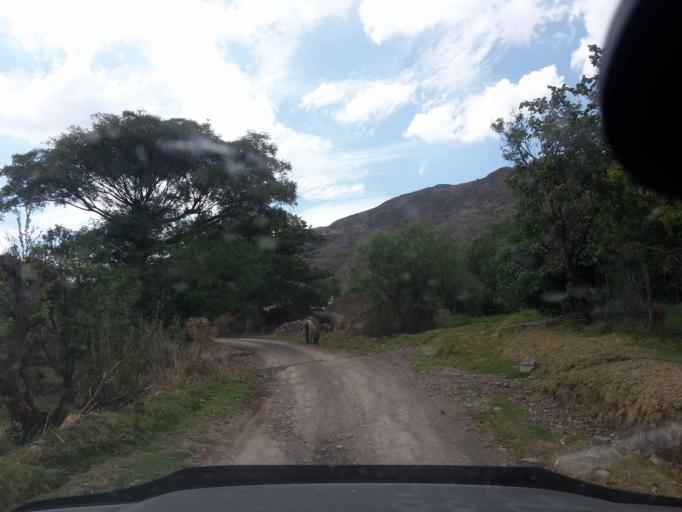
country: BO
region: Cochabamba
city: Colchani
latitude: -17.5155
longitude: -66.6144
